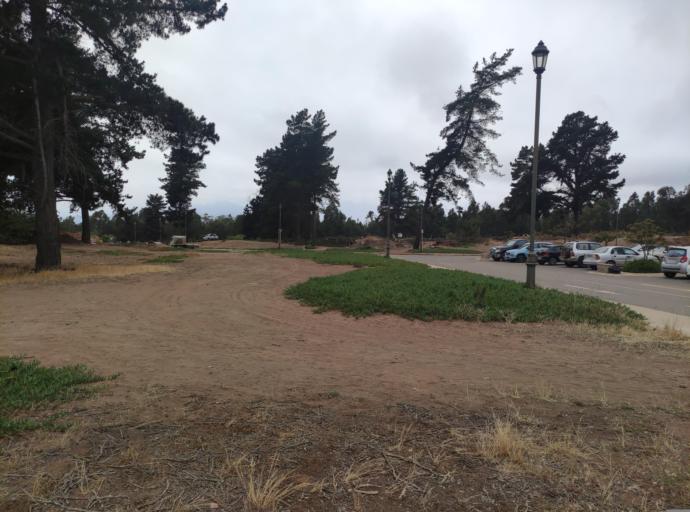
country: CL
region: Valparaiso
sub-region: Provincia de Valparaiso
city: Vina del Mar
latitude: -32.9419
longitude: -71.5192
